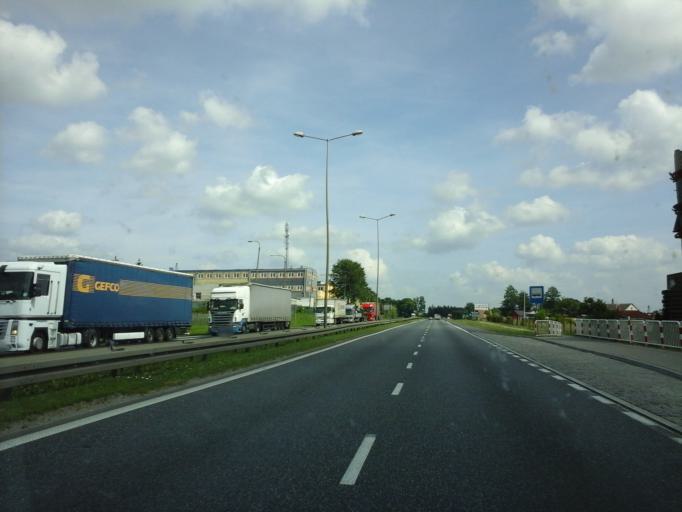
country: PL
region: Lodz Voivodeship
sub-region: Powiat lodzki wschodni
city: Tuszyn
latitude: 51.5998
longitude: 19.5433
